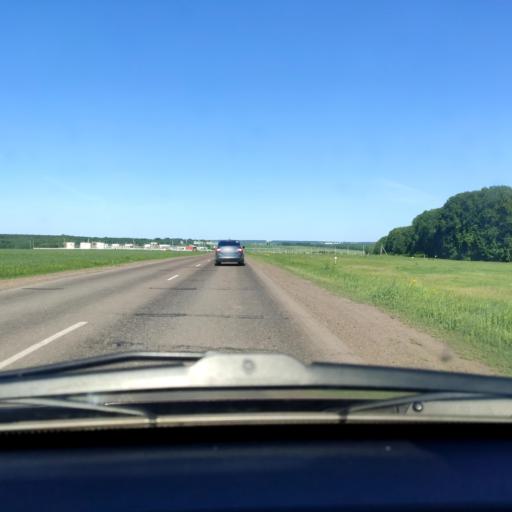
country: RU
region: Bashkortostan
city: Mikhaylovka
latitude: 54.8211
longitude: 55.7513
